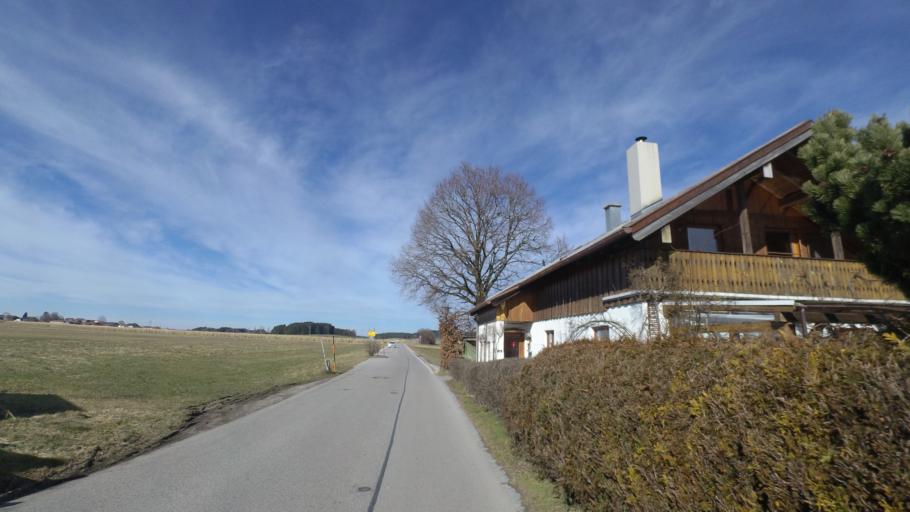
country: DE
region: Bavaria
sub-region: Upper Bavaria
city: Traunstein
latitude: 47.8741
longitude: 12.6217
